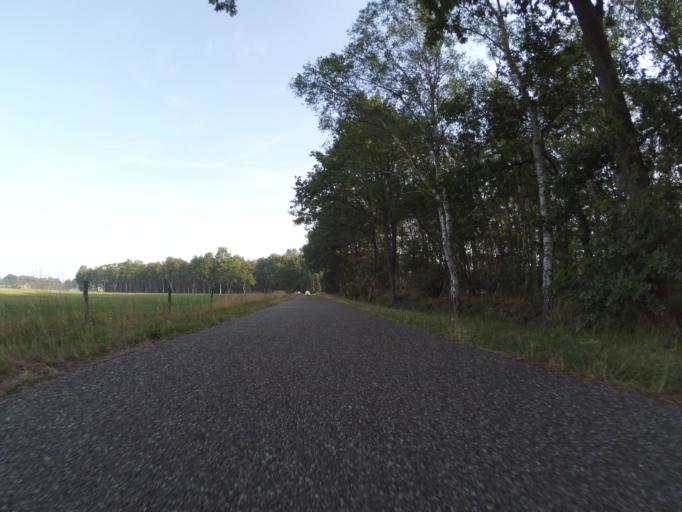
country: NL
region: Overijssel
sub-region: Gemeente Wierden
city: Wierden
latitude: 52.3669
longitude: 6.4968
